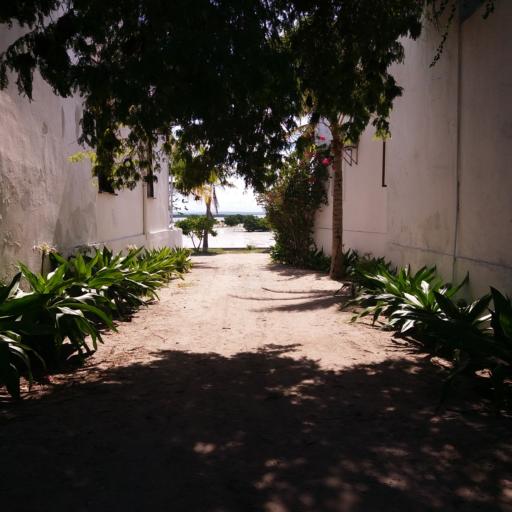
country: MZ
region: Cabo Delgado
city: Pemba
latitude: -12.3425
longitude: 40.5829
